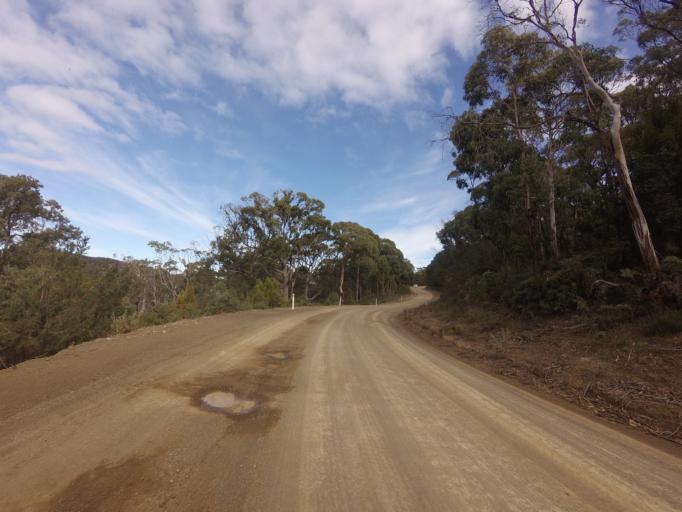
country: AU
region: Tasmania
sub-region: Clarence
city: Sandford
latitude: -43.0931
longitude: 147.7304
